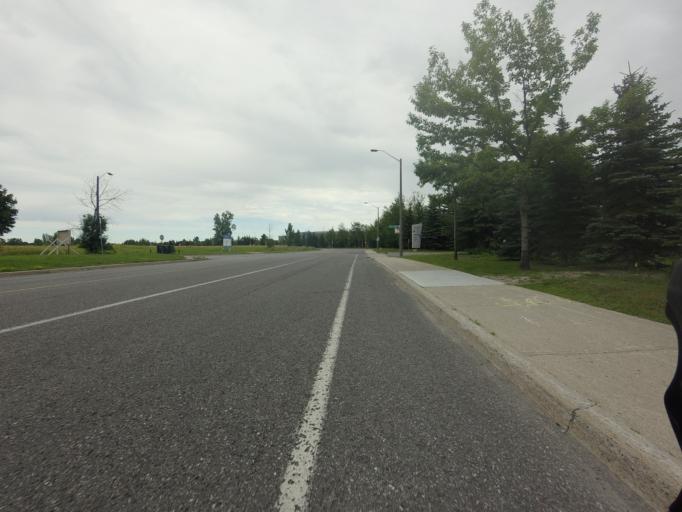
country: CA
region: Ontario
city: Ottawa
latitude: 45.2940
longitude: -75.7084
